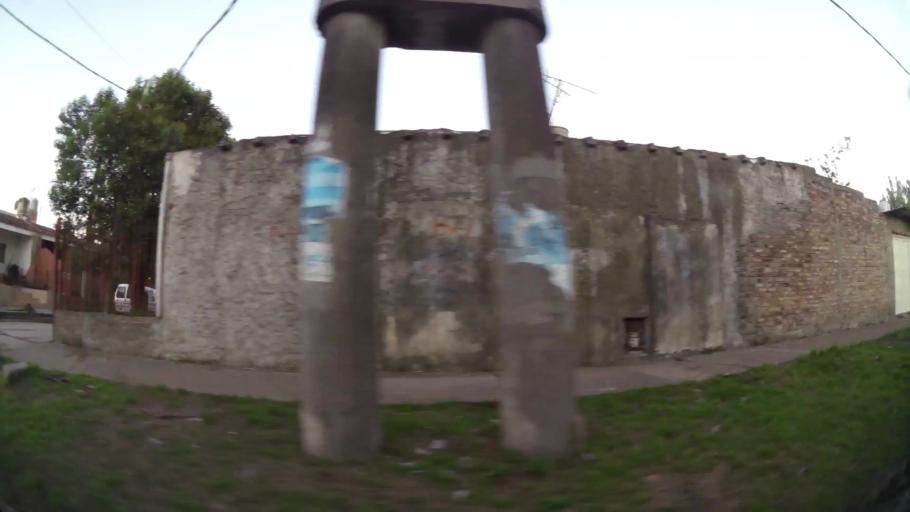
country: AR
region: Buenos Aires
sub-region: Partido de Almirante Brown
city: Adrogue
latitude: -34.7947
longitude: -58.3226
